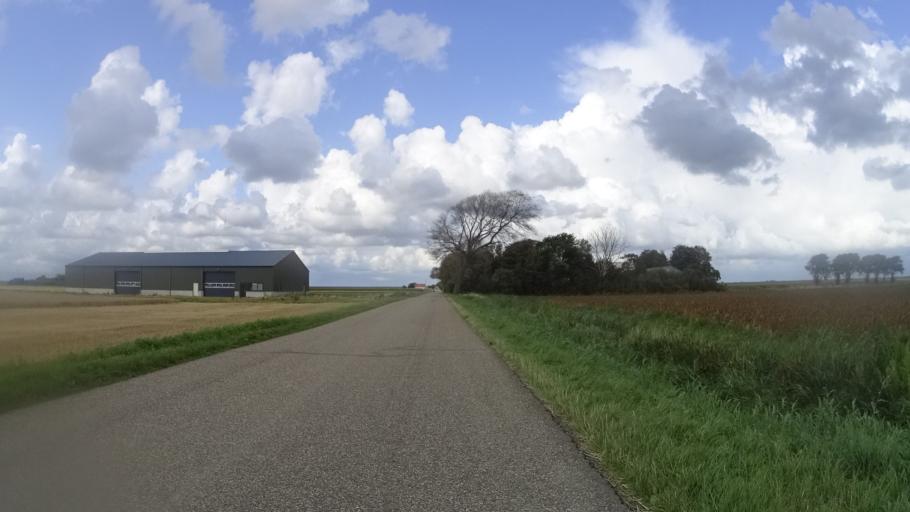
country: NL
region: North Holland
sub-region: Gemeente Schagen
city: Schagen
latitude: 52.8676
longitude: 4.8972
